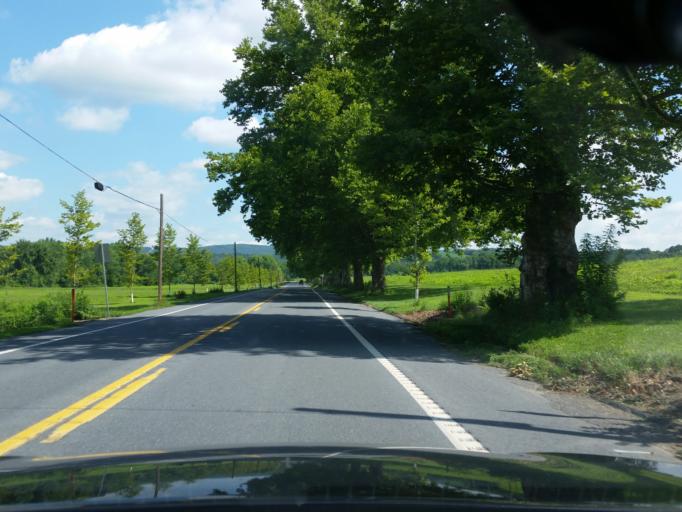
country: US
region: Pennsylvania
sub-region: Dauphin County
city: Matamoras
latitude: 40.4755
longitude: -76.9315
